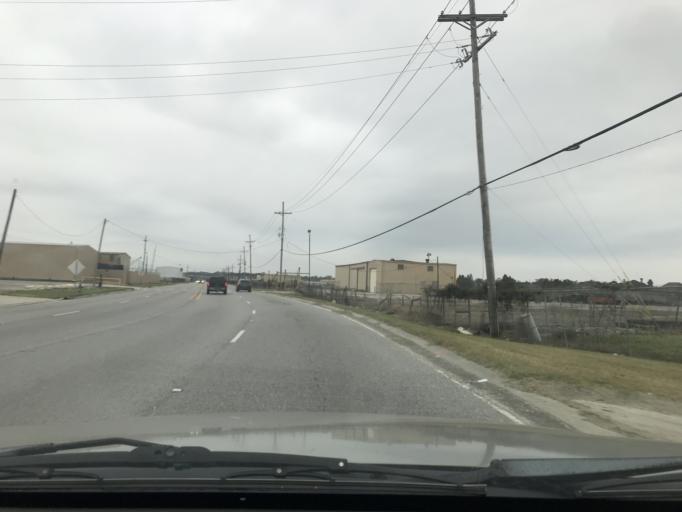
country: US
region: Louisiana
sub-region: Jefferson Parish
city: Harvey
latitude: 29.8816
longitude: -90.0758
